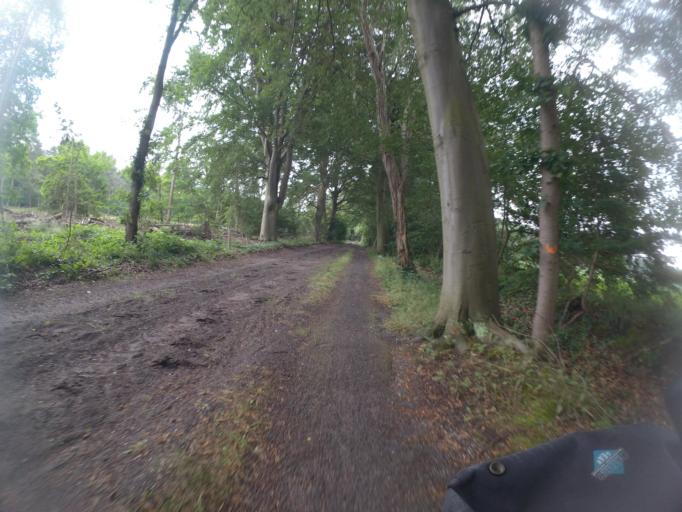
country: NL
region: Drenthe
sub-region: Gemeente Westerveld
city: Dwingeloo
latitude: 52.8119
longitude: 6.3492
